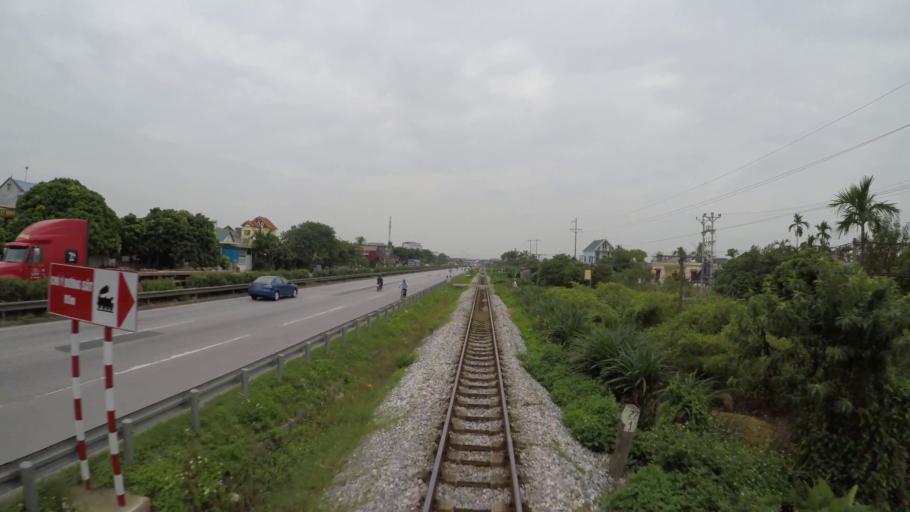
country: VN
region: Hai Duong
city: Phu Thai
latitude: 20.9715
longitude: 106.4714
